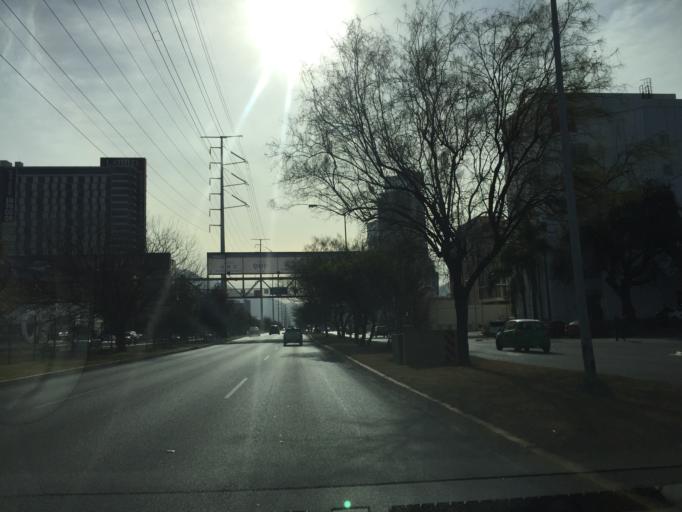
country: MX
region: Nuevo Leon
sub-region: Monterrey
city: Monterrey
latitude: 25.6482
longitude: -100.3286
